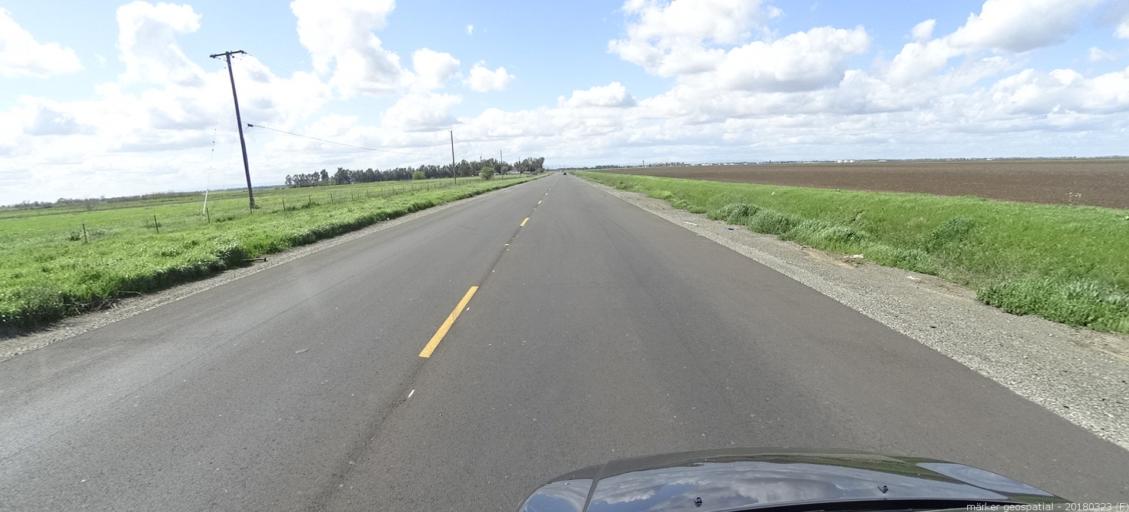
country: US
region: California
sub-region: Sacramento County
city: Elverta
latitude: 38.6856
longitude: -121.5494
